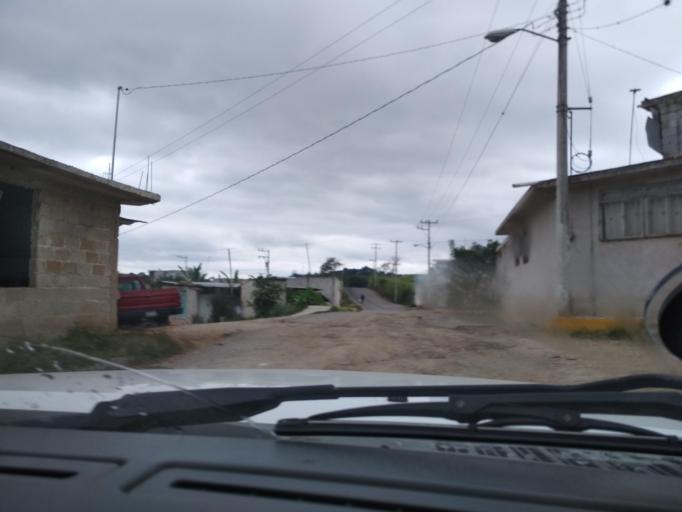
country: MX
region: Veracruz
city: El Castillo
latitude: 19.5715
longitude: -96.8515
